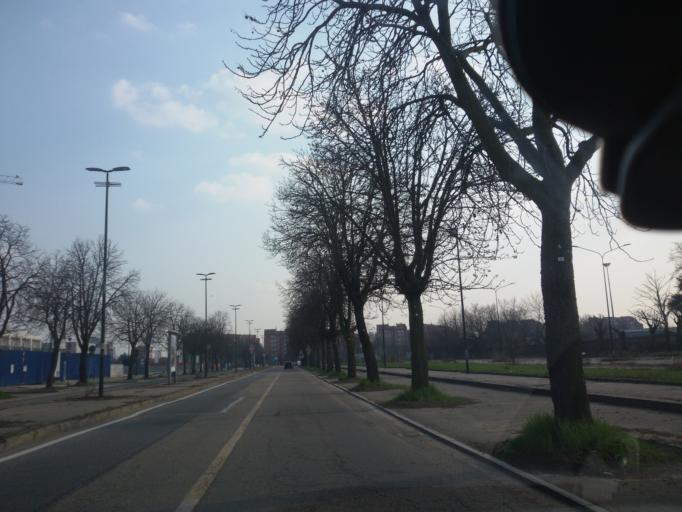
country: IT
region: Piedmont
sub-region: Provincia di Torino
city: Savonera
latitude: 45.1113
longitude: 7.6294
